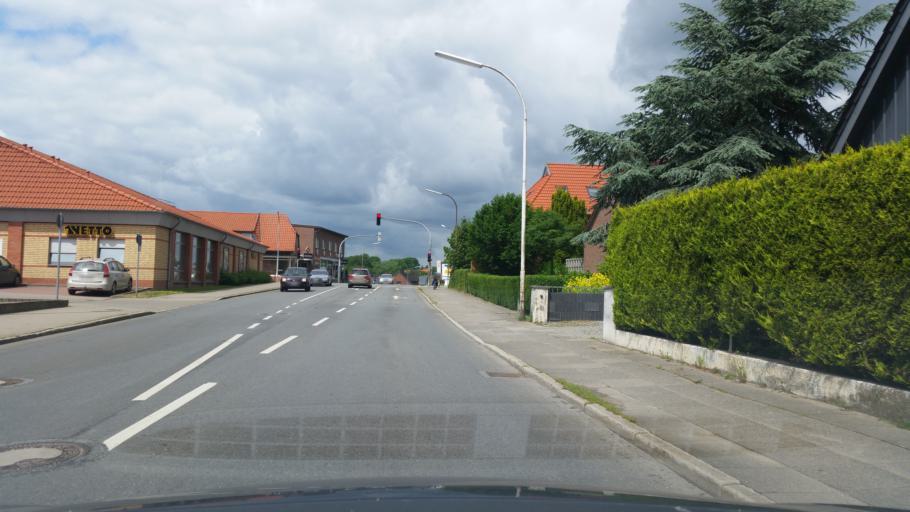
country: DE
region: Schleswig-Holstein
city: Eutin
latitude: 54.1305
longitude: 10.6175
